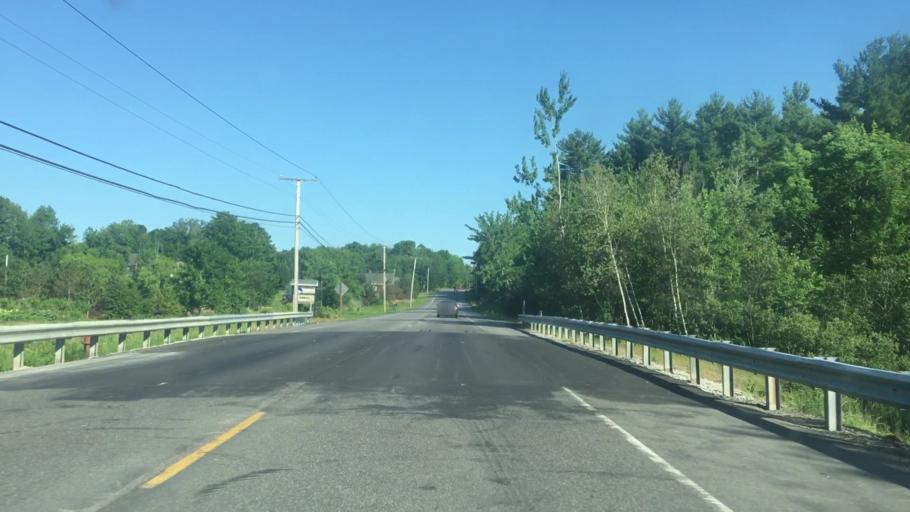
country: US
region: Maine
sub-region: York County
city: Buxton
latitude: 43.7084
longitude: -70.5098
